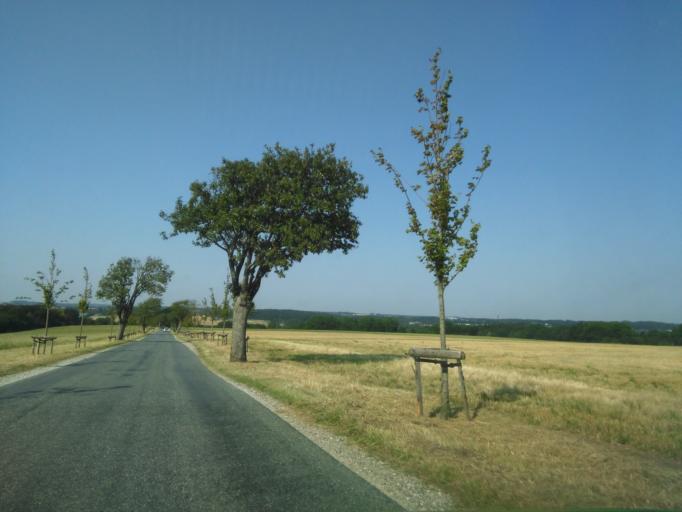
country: DK
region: Central Jutland
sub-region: Arhus Kommune
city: Kolt
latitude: 56.1314
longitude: 10.0790
